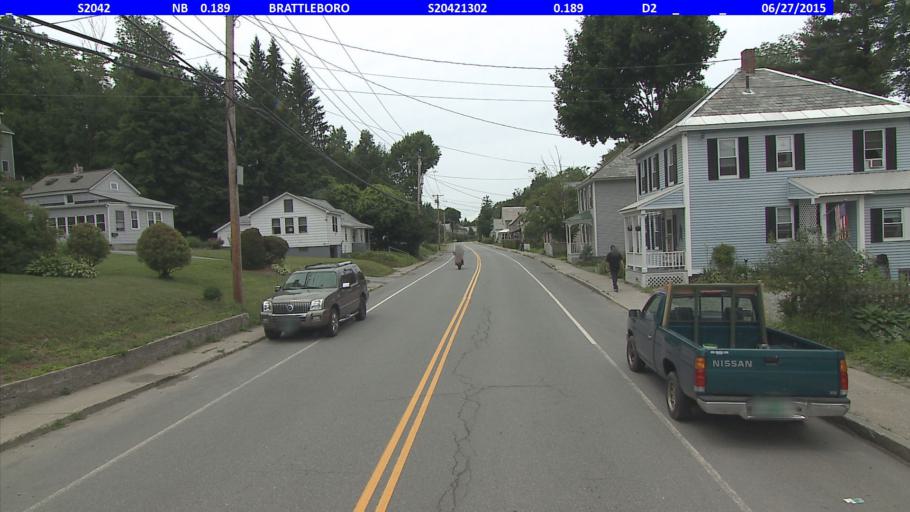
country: US
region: Vermont
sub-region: Windham County
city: Brattleboro
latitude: 42.8401
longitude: -72.5552
